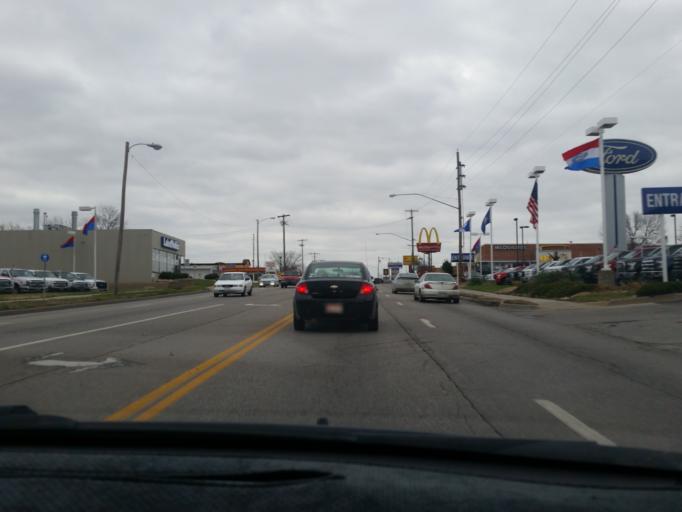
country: US
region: Kansas
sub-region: Douglas County
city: Lawrence
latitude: 38.9428
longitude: -95.2464
